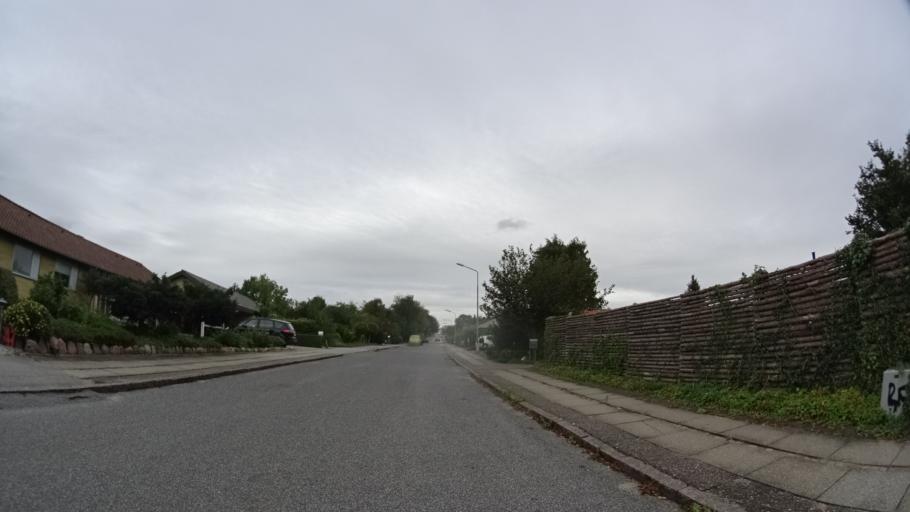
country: DK
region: Central Jutland
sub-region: Arhus Kommune
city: Arhus
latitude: 56.1603
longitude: 10.1624
